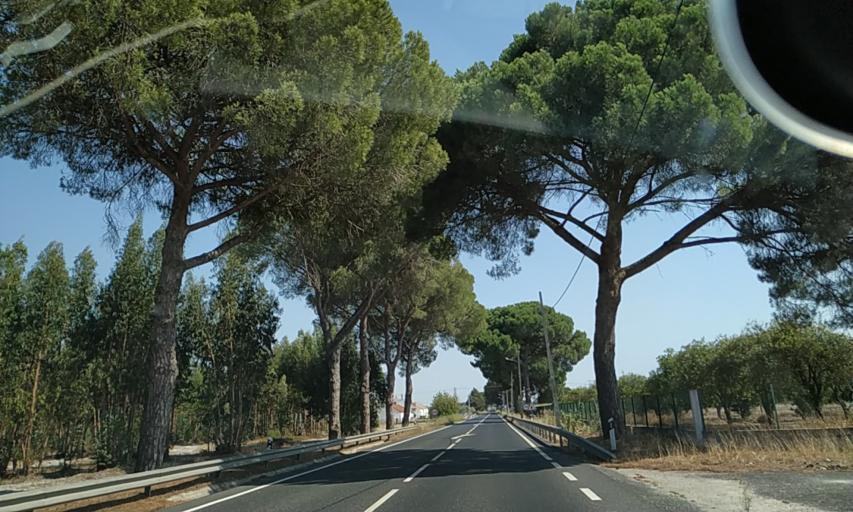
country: PT
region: Santarem
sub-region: Benavente
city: Poceirao
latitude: 38.7349
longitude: -8.6521
